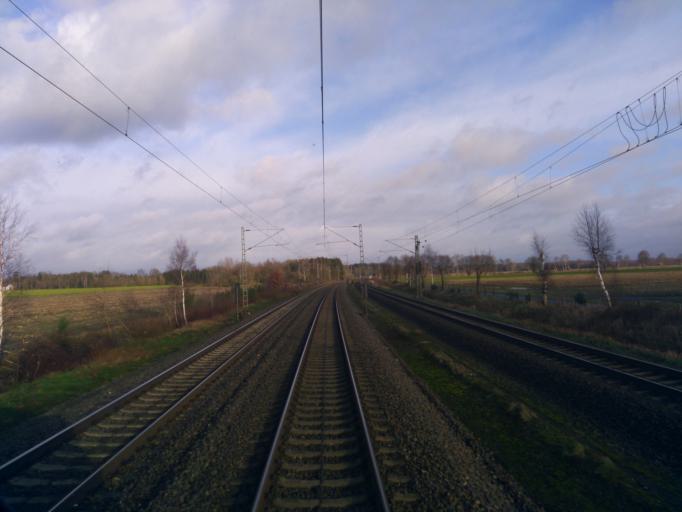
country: DE
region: Lower Saxony
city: Scheessel
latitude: 53.1832
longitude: 9.5208
